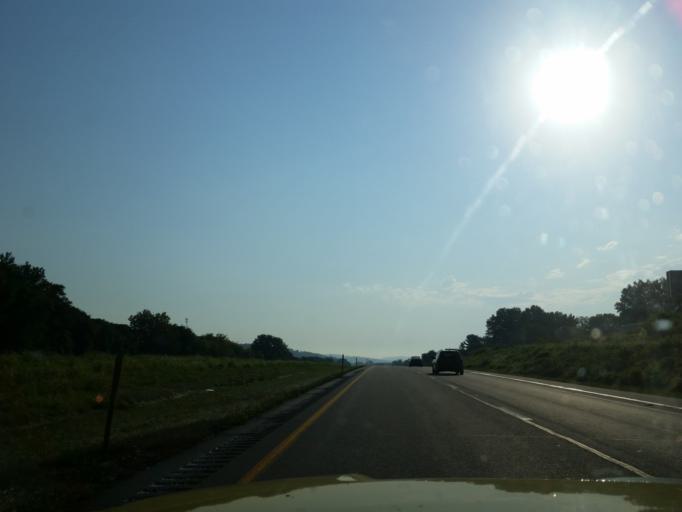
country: US
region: Pennsylvania
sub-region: York County
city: Hallam
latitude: 40.0227
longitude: -76.5705
